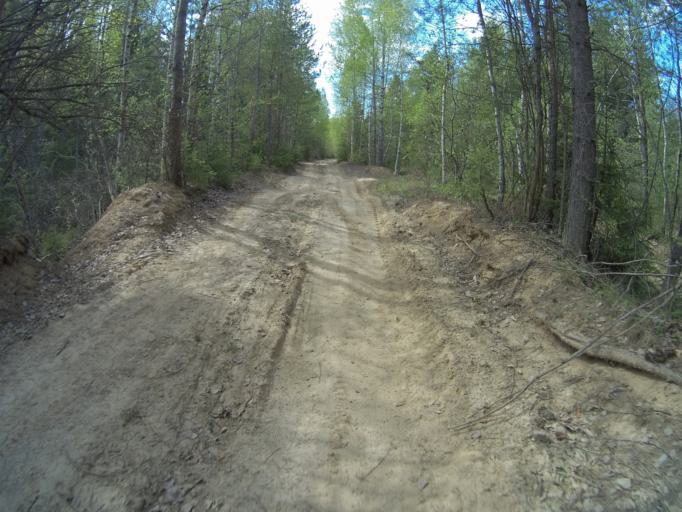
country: RU
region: Vladimir
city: Raduzhnyy
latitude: 55.9671
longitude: 40.2335
